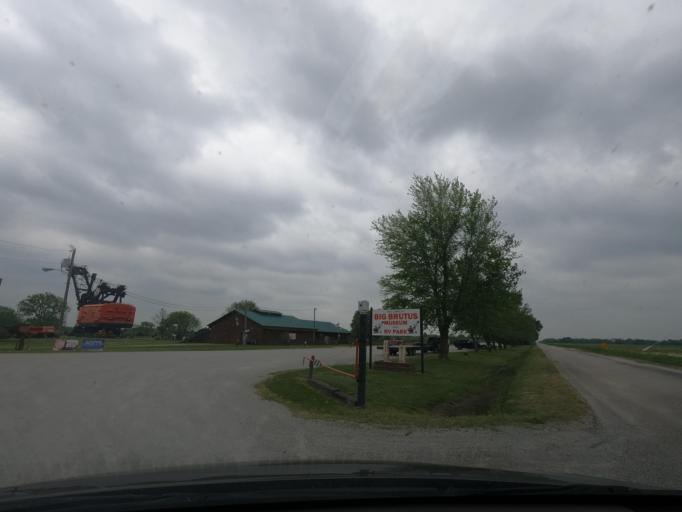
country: US
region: Kansas
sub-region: Cherokee County
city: Columbus
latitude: 37.2743
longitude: -94.9406
